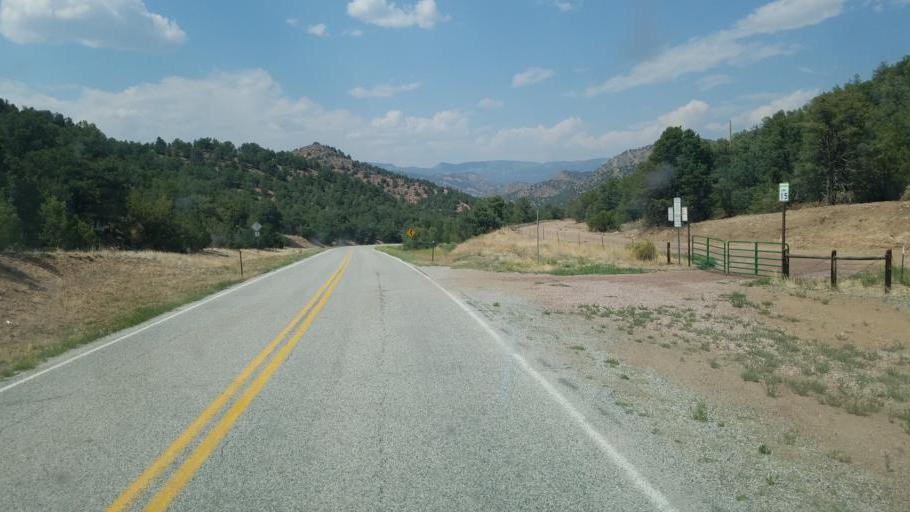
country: US
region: Colorado
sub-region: Custer County
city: Westcliffe
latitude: 38.3759
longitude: -105.5840
